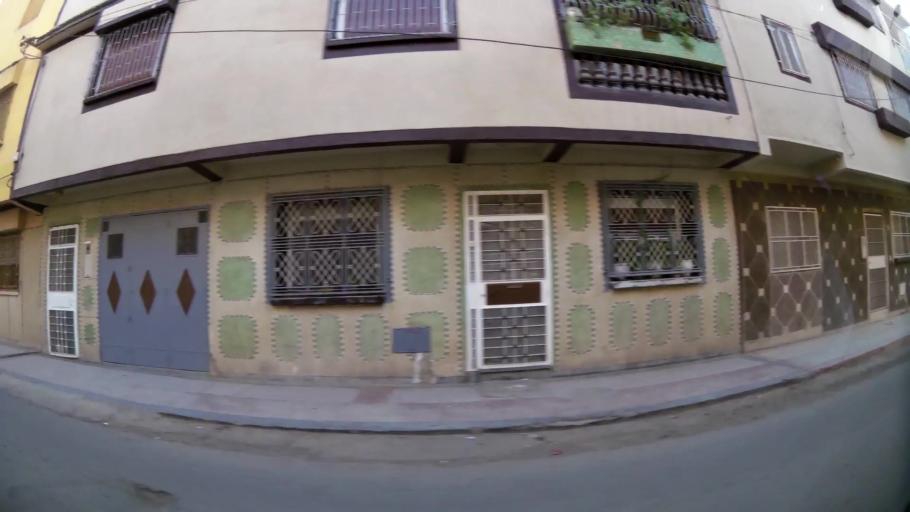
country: MA
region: Oriental
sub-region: Oujda-Angad
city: Oujda
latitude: 34.6781
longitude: -1.9003
